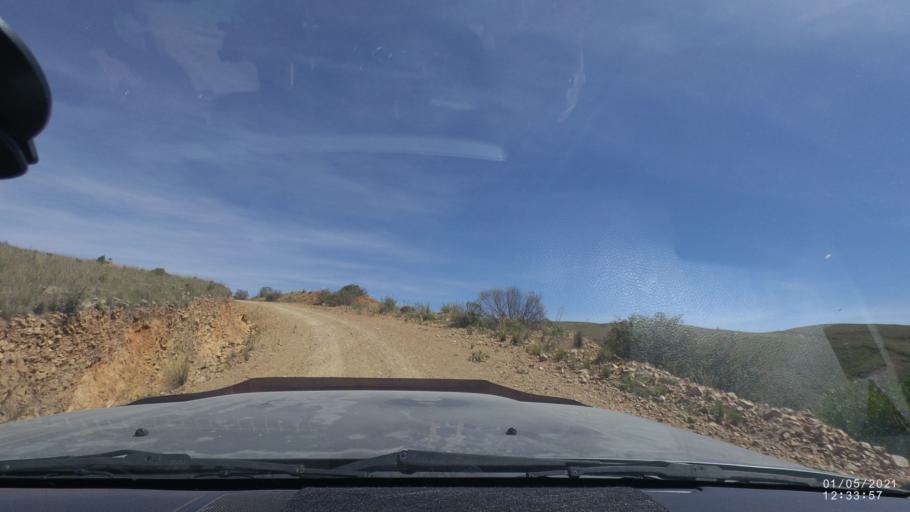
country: BO
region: Cochabamba
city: Capinota
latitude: -17.6750
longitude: -66.1487
